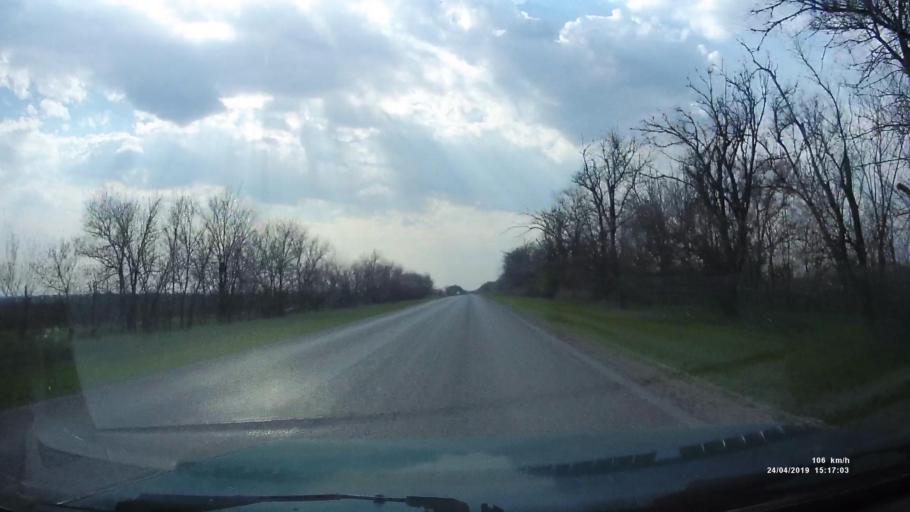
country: RU
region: Rostov
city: Remontnoye
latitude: 46.5465
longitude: 43.1984
